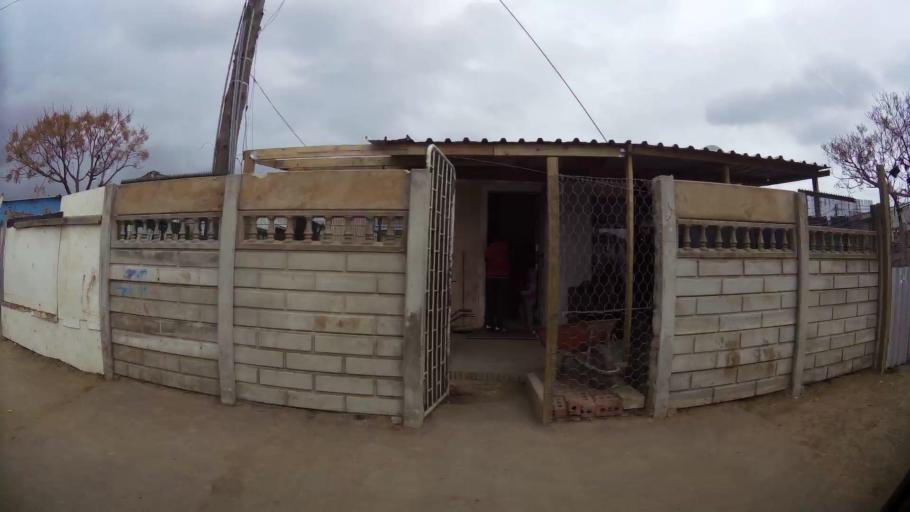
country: ZA
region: Eastern Cape
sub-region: Nelson Mandela Bay Metropolitan Municipality
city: Port Elizabeth
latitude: -33.8855
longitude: 25.5542
